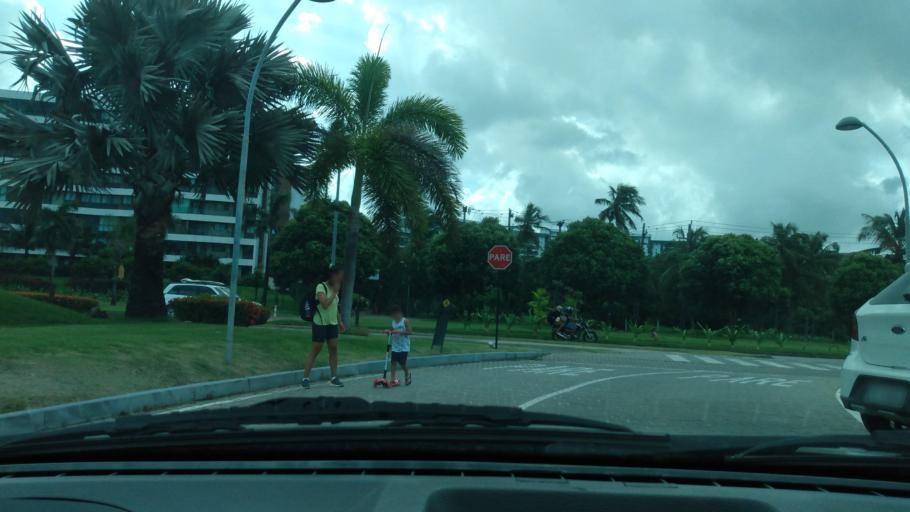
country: BR
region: Pernambuco
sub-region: Jaboatao Dos Guararapes
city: Jaboatao
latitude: -8.2531
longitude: -34.9441
